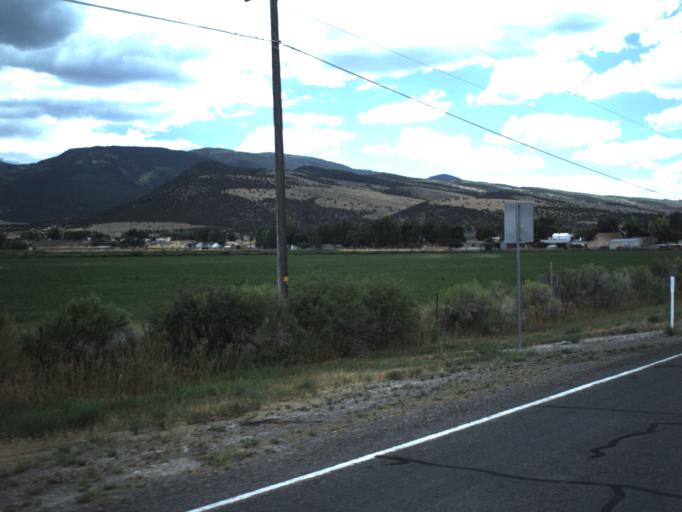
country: US
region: Utah
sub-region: Sanpete County
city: Centerfield
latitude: 39.1224
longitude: -111.7118
